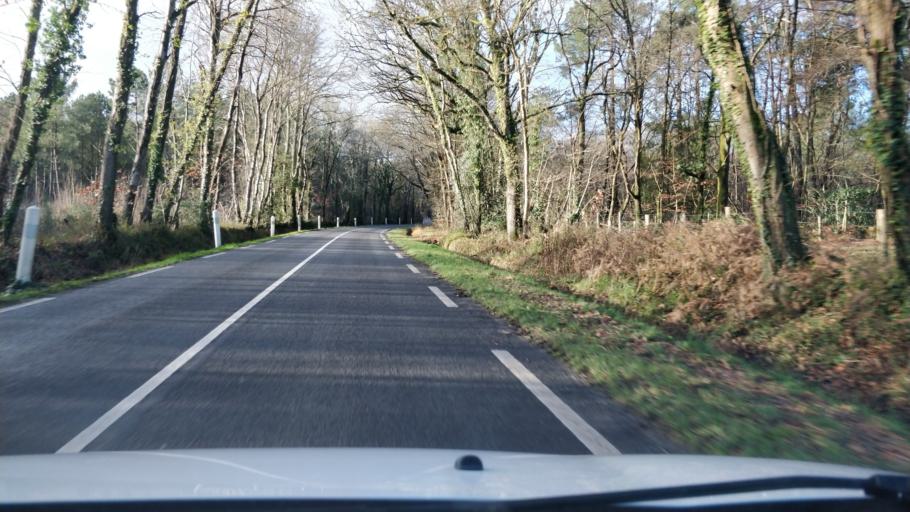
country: FR
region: Pays de la Loire
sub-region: Departement de la Loire-Atlantique
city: Herbignac
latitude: 47.4362
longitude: -2.3410
